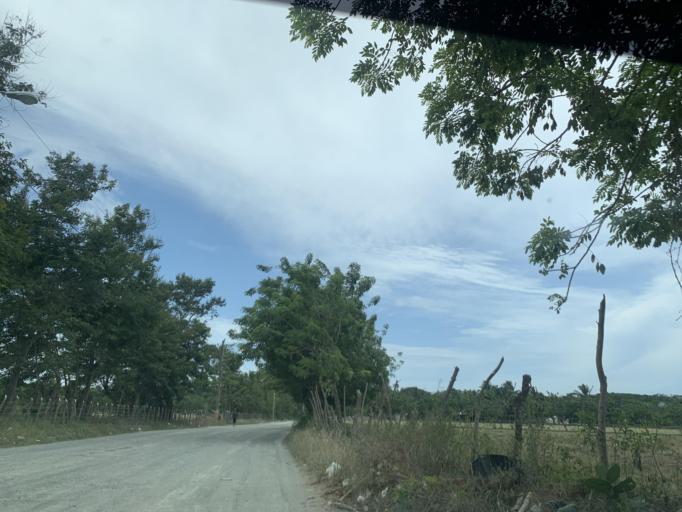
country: DO
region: Puerto Plata
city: Imbert
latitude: 19.8214
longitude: -70.7827
